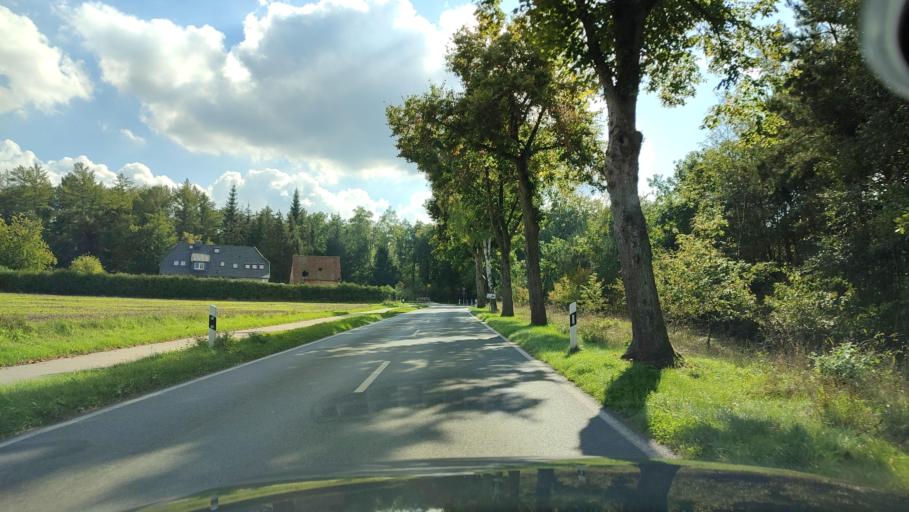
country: DE
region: Lower Saxony
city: Bad Fallingbostel
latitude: 52.8698
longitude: 9.6678
